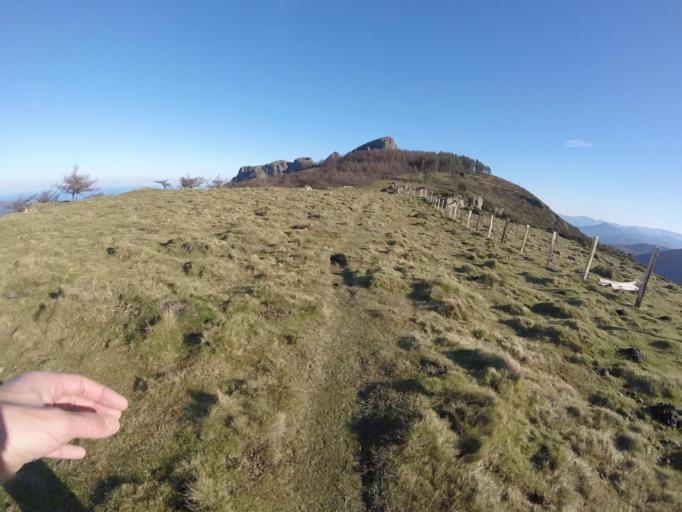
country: ES
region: Basque Country
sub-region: Provincia de Guipuzcoa
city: Irun
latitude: 43.2766
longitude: -1.7940
